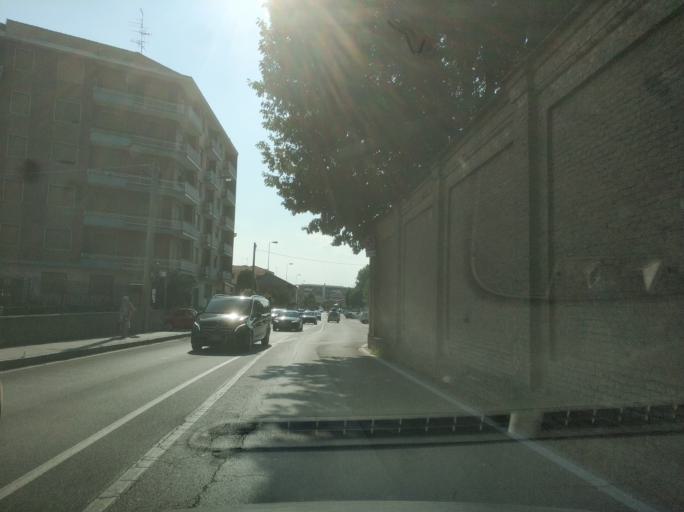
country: IT
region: Piedmont
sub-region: Provincia di Cuneo
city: Bra
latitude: 44.7020
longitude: 7.8456
